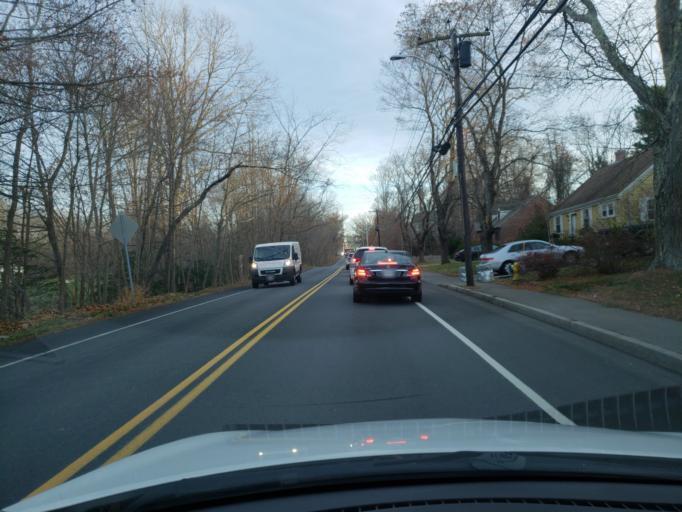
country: US
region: Massachusetts
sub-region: Essex County
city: Andover
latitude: 42.6631
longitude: -71.1689
